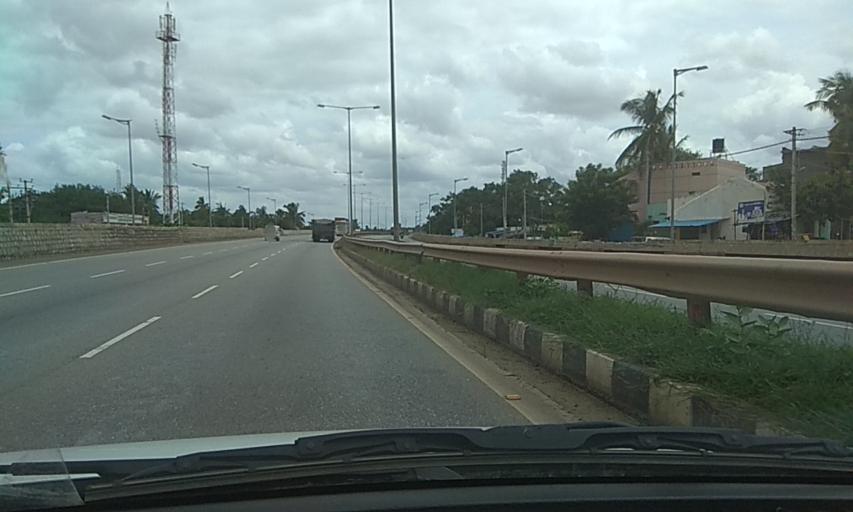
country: IN
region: Karnataka
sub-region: Tumkur
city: Sira
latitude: 13.7971
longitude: 76.8027
